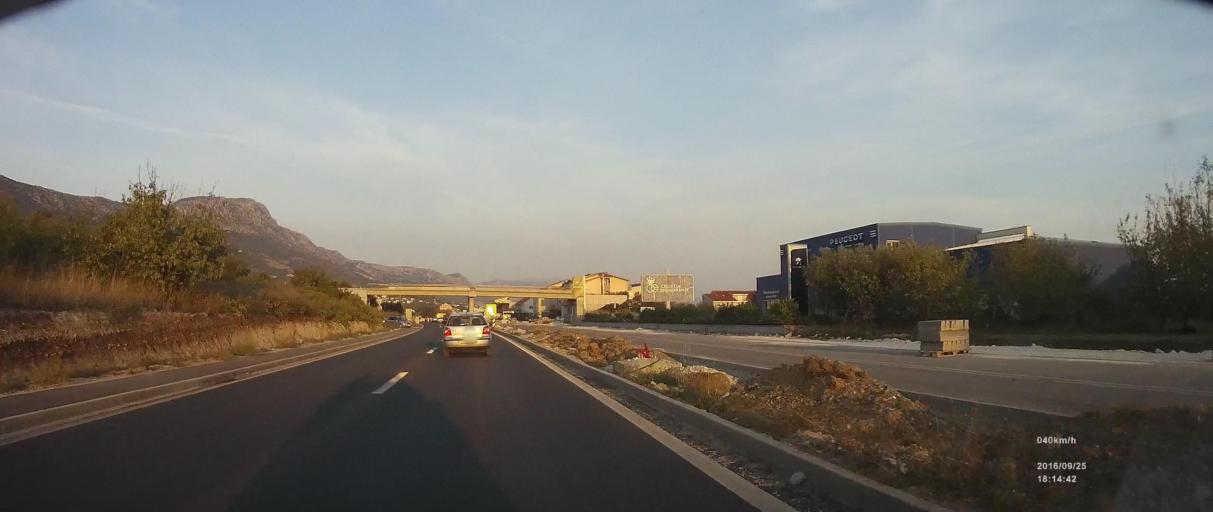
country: HR
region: Splitsko-Dalmatinska
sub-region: Grad Split
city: Split
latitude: 43.5582
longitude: 16.3512
